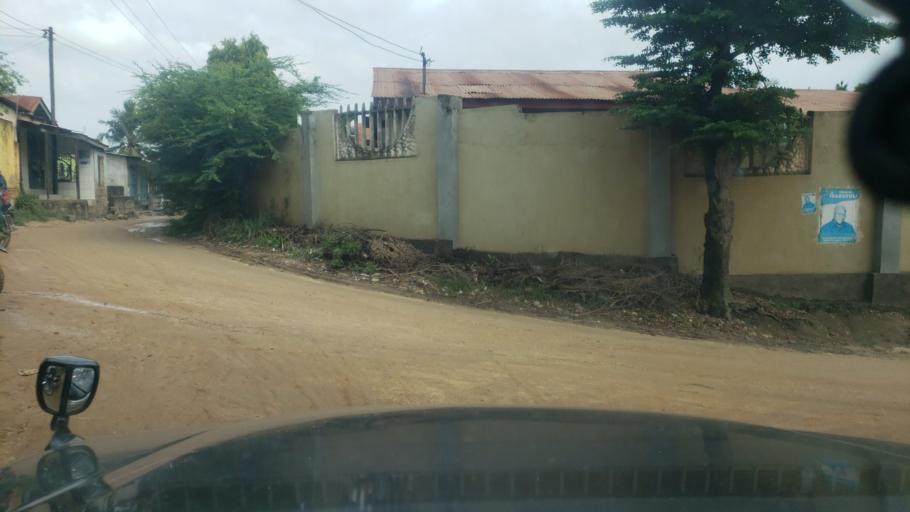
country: TZ
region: Pwani
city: Vikindu
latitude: -6.9200
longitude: 39.2548
